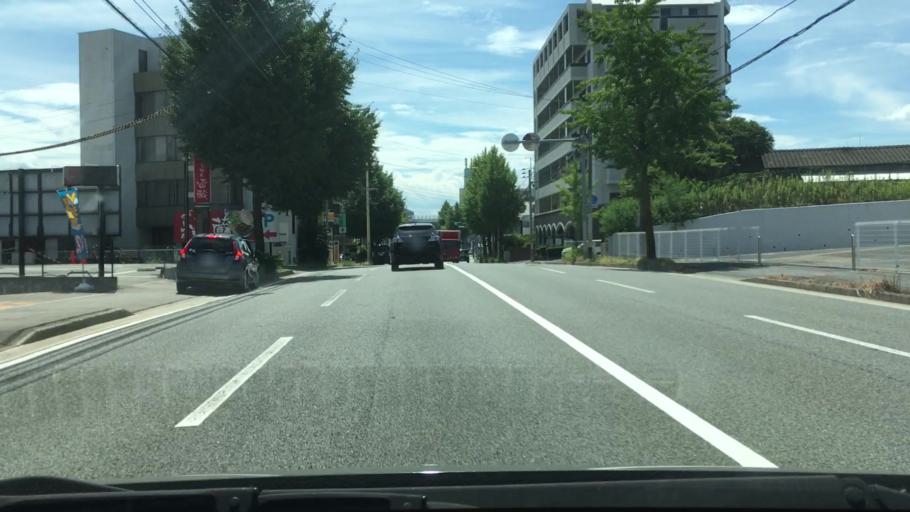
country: JP
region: Fukuoka
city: Onojo
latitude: 33.5585
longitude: 130.4503
